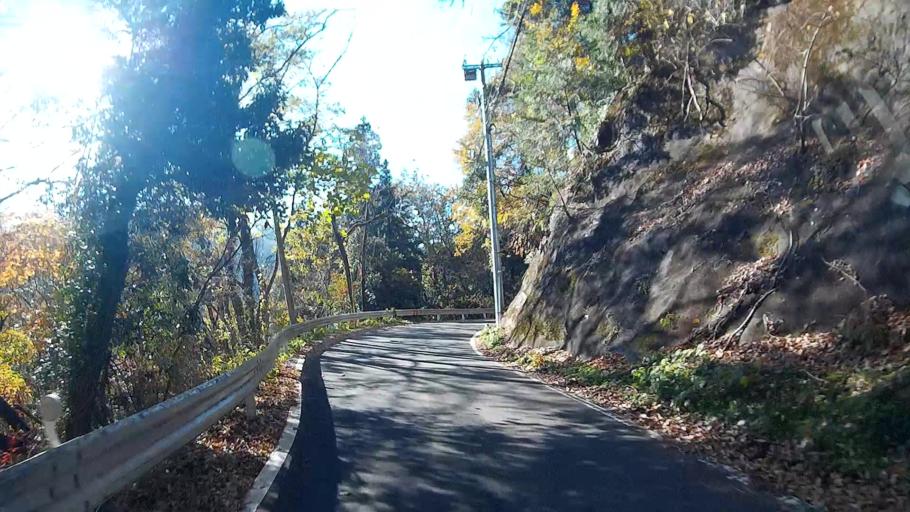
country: JP
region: Yamanashi
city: Uenohara
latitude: 35.5879
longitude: 139.1332
